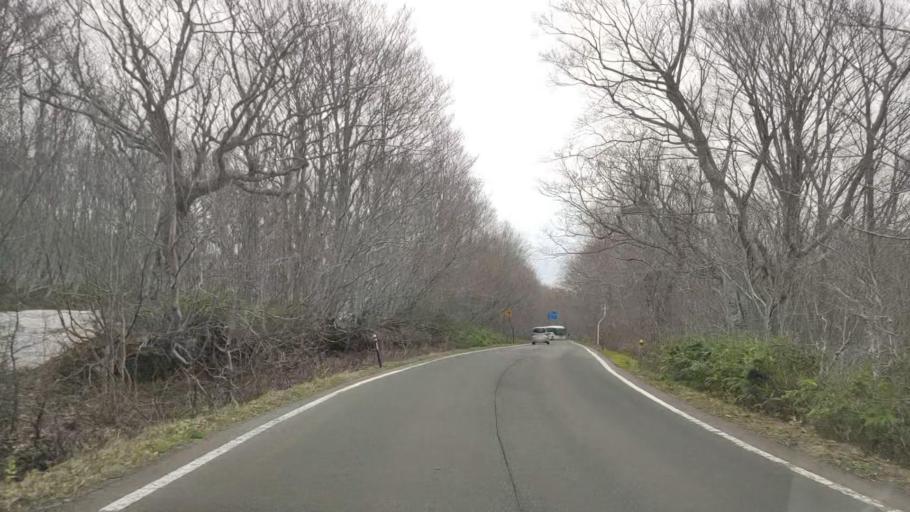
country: JP
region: Aomori
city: Aomori Shi
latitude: 40.6655
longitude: 140.9564
